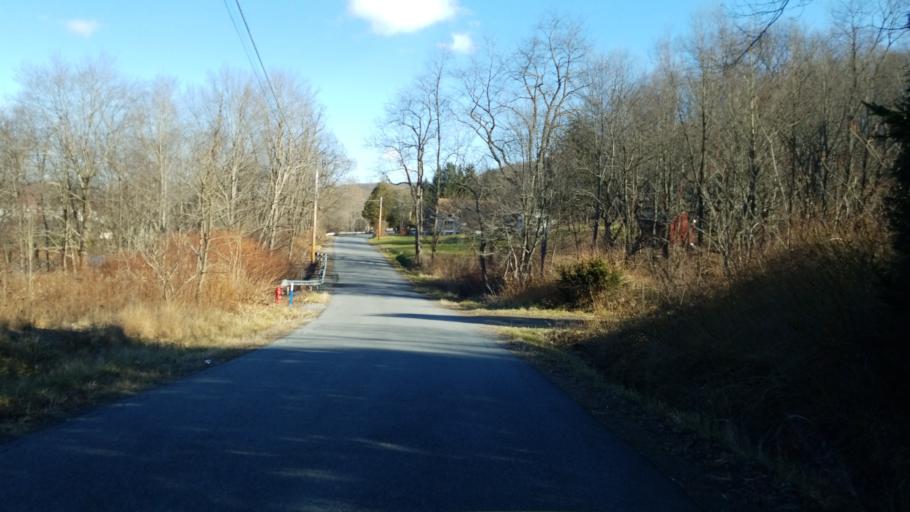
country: US
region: Pennsylvania
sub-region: Clearfield County
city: Hyde
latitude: 40.9882
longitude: -78.4704
